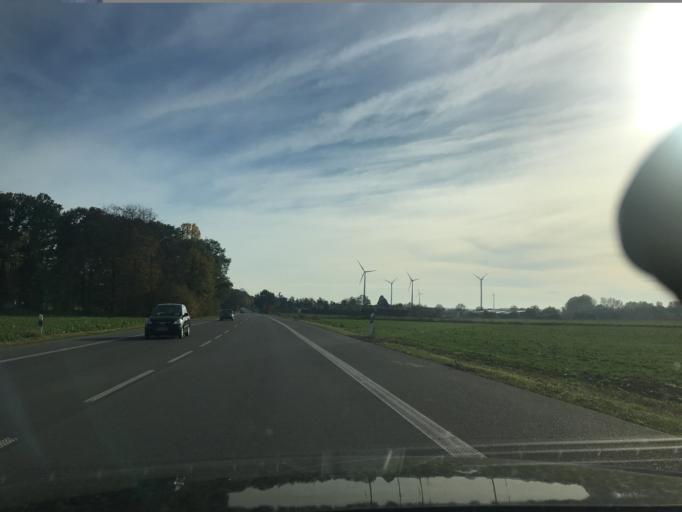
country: DE
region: North Rhine-Westphalia
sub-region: Regierungsbezirk Dusseldorf
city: Grefrath
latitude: 51.3675
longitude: 6.3113
